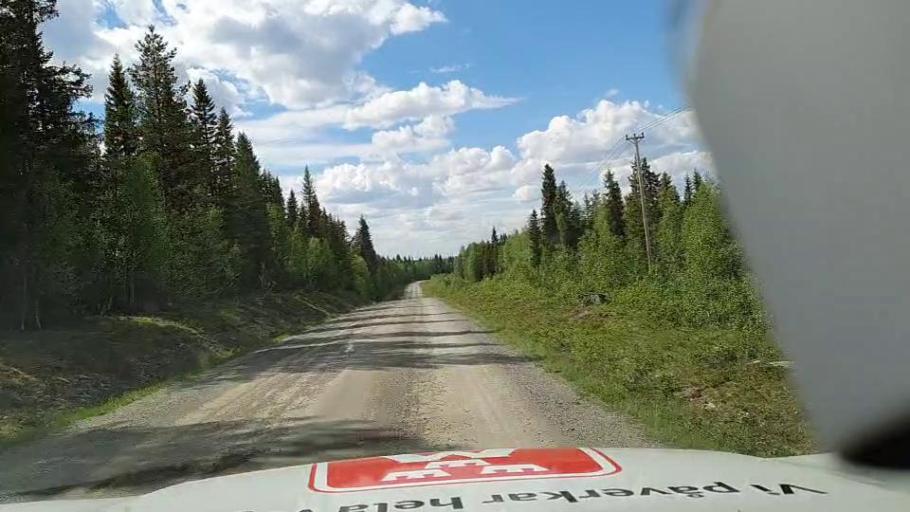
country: SE
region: Vaesterbotten
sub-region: Vilhelmina Kommun
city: Sjoberg
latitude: 64.5421
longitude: 15.6644
